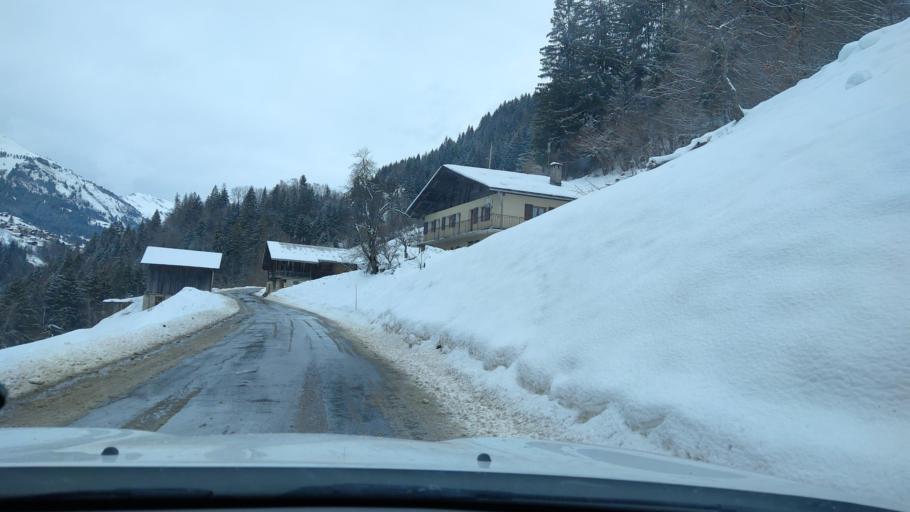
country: FR
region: Rhone-Alpes
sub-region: Departement de la Savoie
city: Beaufort
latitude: 45.7337
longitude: 6.5742
